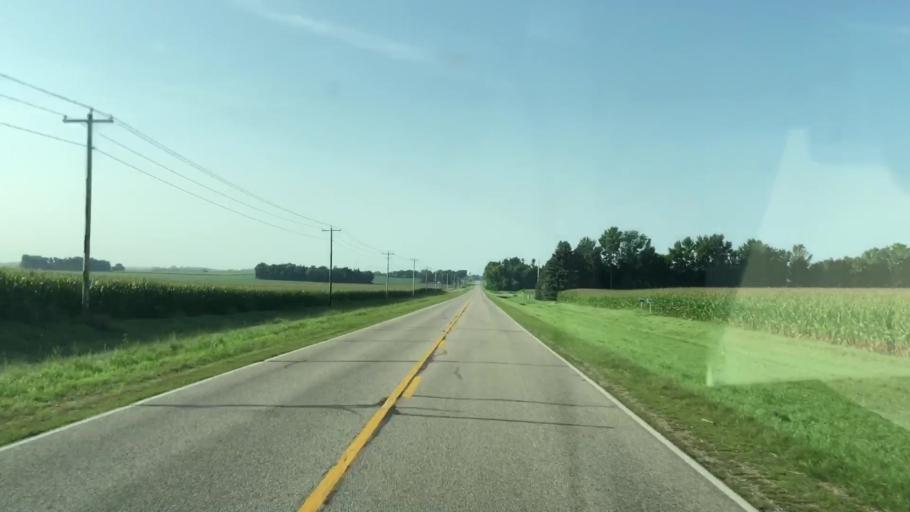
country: US
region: Iowa
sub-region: Lyon County
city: George
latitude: 43.3715
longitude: -95.9982
